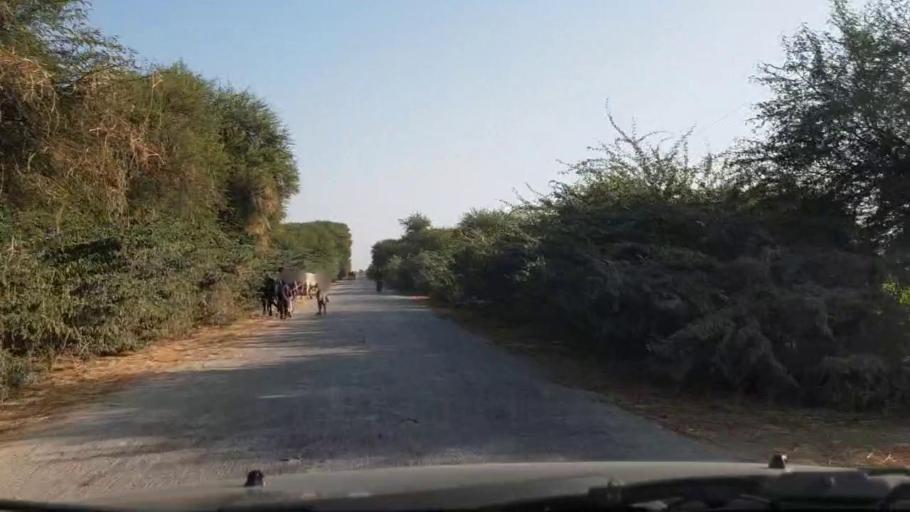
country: PK
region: Sindh
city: Tando Bago
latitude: 24.8024
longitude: 68.9853
